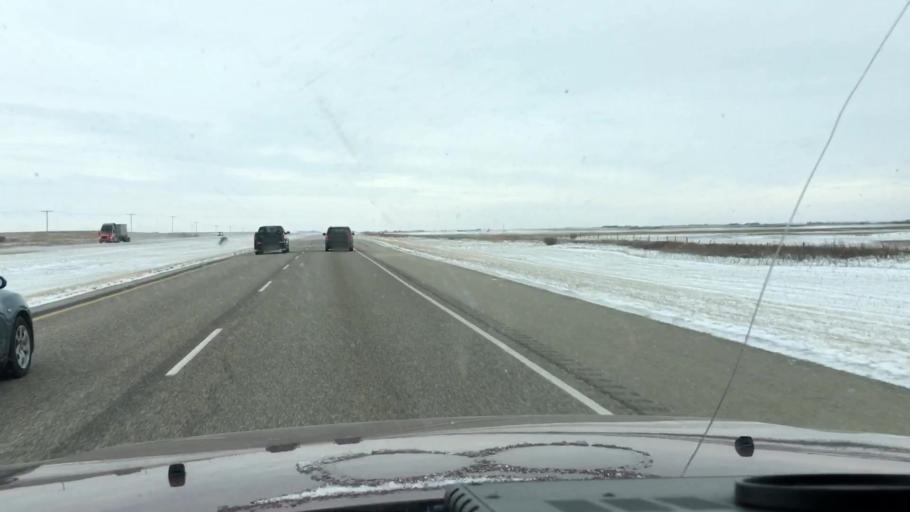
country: CA
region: Saskatchewan
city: Saskatoon
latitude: 51.5992
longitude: -106.3945
